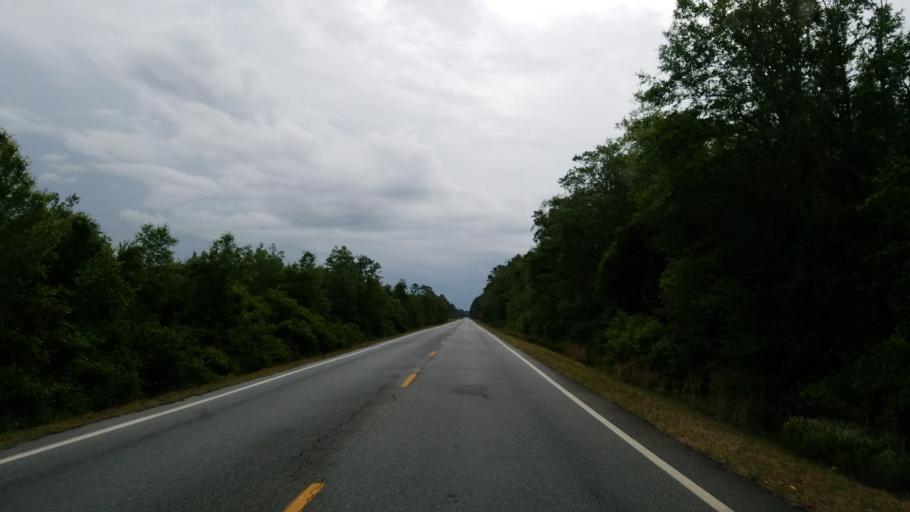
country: US
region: Georgia
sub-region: Berrien County
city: Ray City
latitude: 31.0829
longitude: -83.2320
